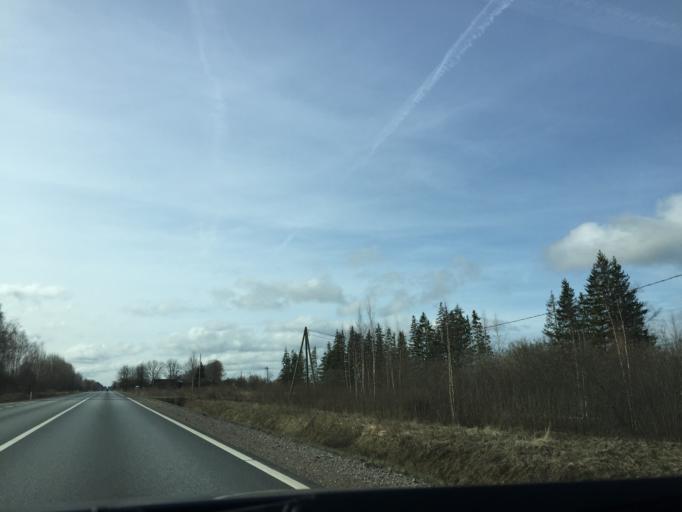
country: LV
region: Jelgava
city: Jelgava
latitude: 56.4651
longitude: 23.6931
